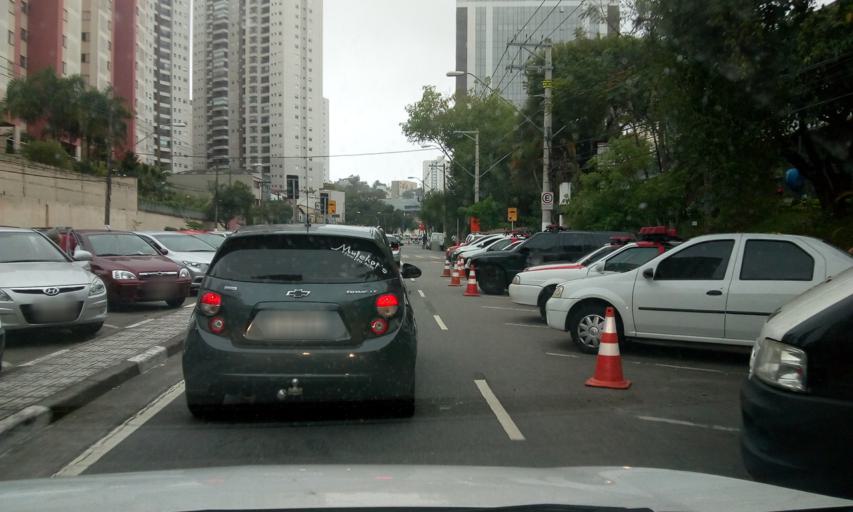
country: BR
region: Sao Paulo
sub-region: Sao Bernardo Do Campo
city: Sao Bernardo do Campo
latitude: -23.6981
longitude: -46.5469
